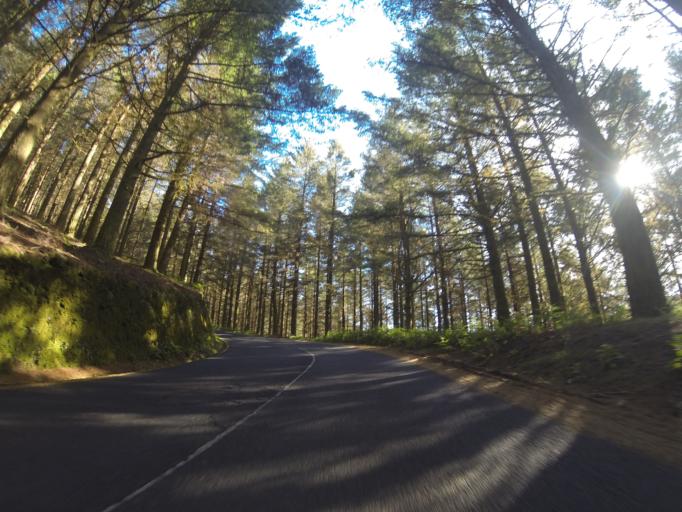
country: PT
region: Madeira
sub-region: Funchal
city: Nossa Senhora do Monte
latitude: 32.7161
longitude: -16.8861
